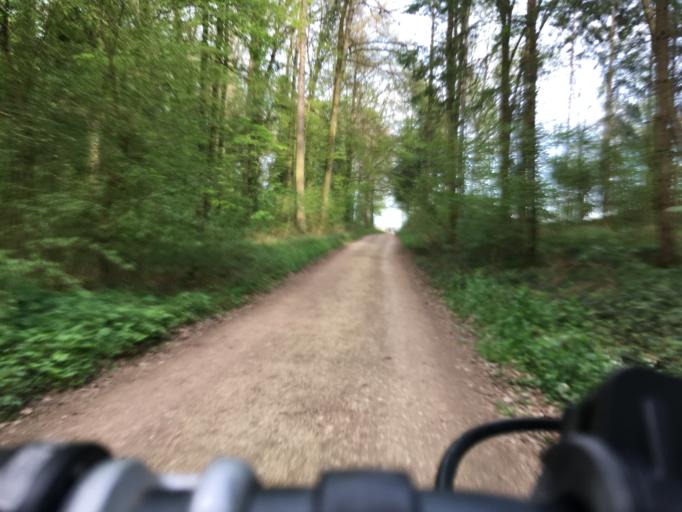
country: DE
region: Baden-Wuerttemberg
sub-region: Freiburg Region
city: Gottmadingen
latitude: 47.7403
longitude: 8.7536
